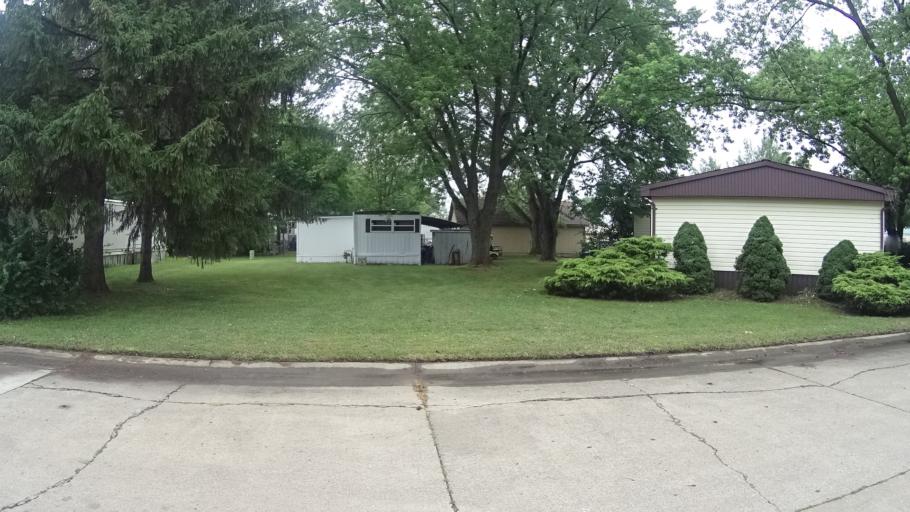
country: US
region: Ohio
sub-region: Erie County
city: Sandusky
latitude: 41.4377
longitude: -82.6652
